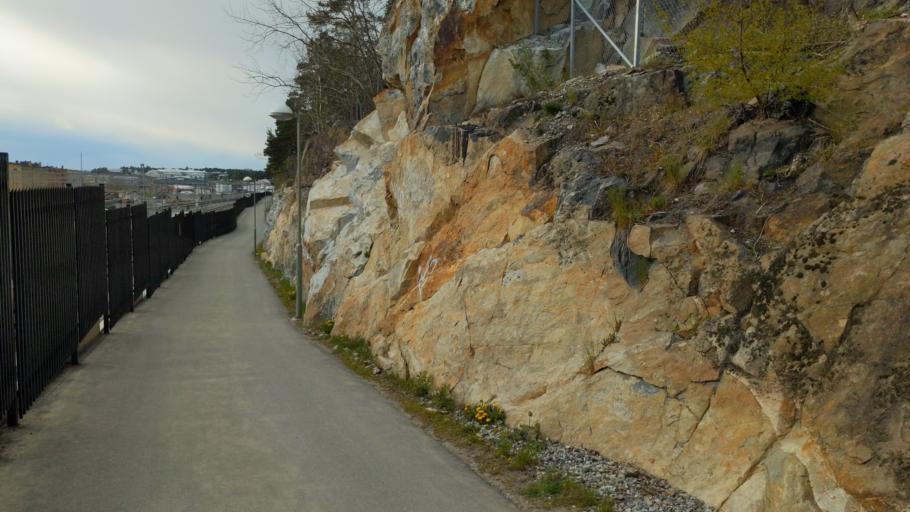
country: SE
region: Stockholm
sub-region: Stockholms Kommun
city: Kista
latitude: 59.3839
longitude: 17.8983
